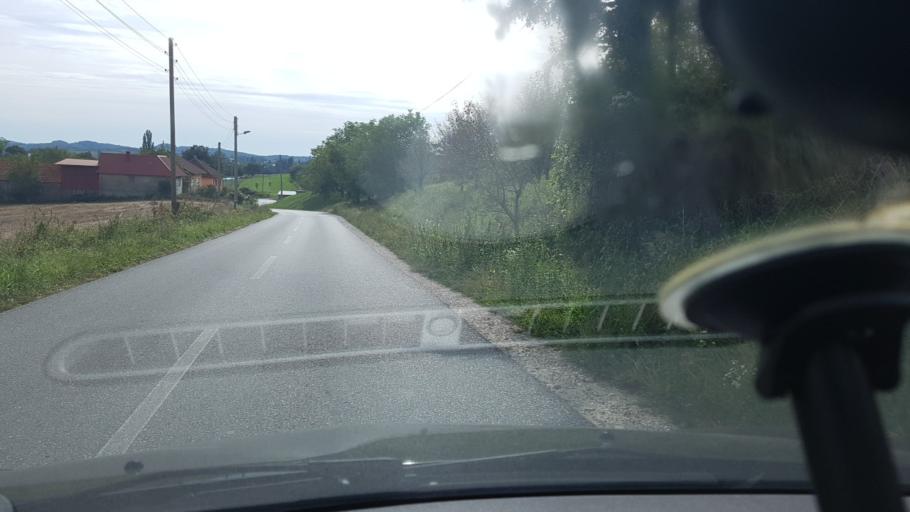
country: HR
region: Varazdinska
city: Ljubescica
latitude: 46.1186
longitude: 16.4224
